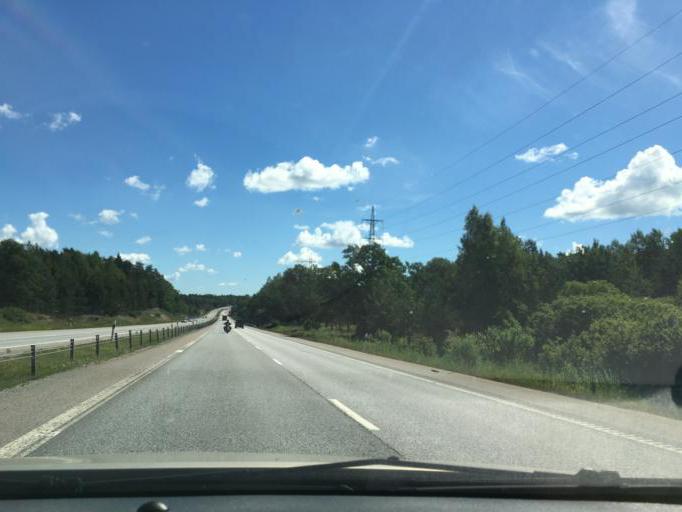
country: SE
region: Stockholm
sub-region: Nacka Kommun
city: Alta
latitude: 59.2927
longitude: 18.2191
